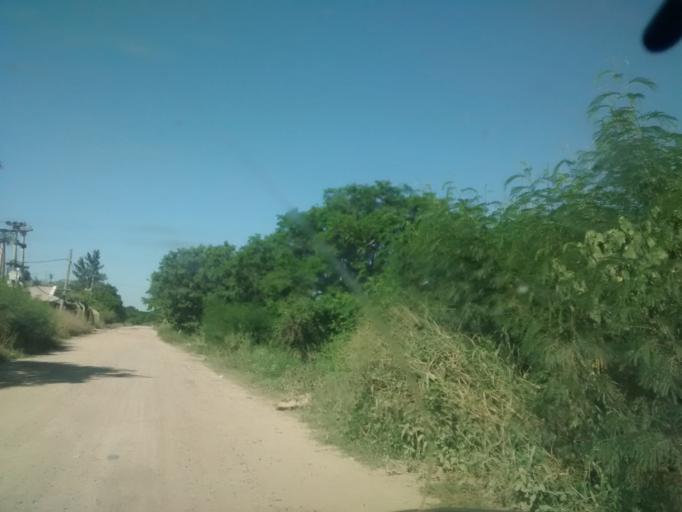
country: AR
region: Chaco
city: Resistencia
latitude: -27.4400
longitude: -58.9598
